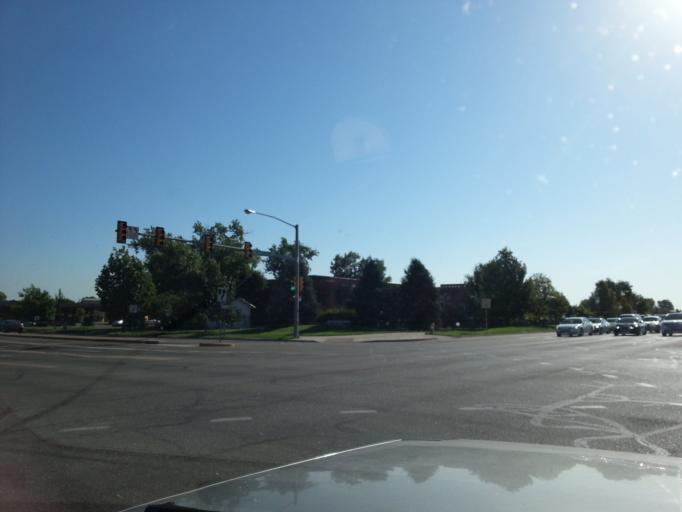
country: US
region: Colorado
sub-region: Larimer County
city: Fort Collins
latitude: 40.5233
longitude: -105.0396
